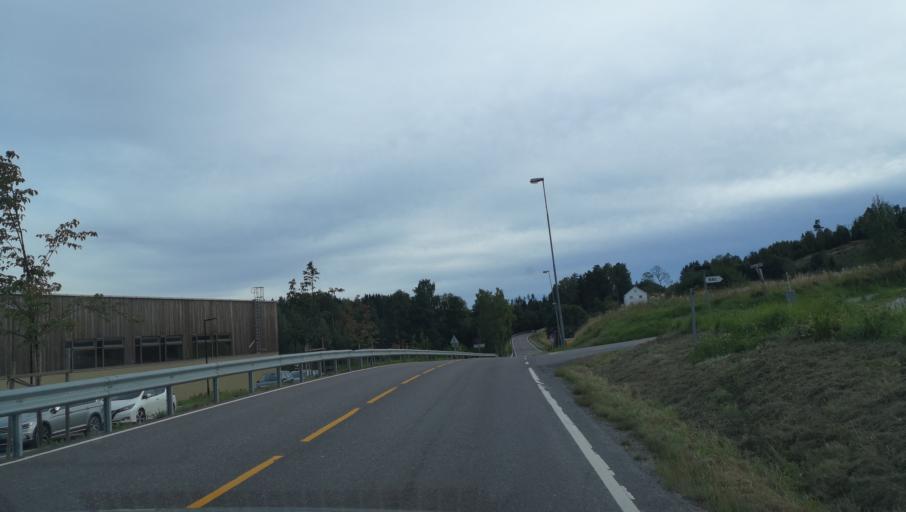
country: NO
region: Ostfold
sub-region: Hobol
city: Tomter
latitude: 59.7210
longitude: 11.0556
